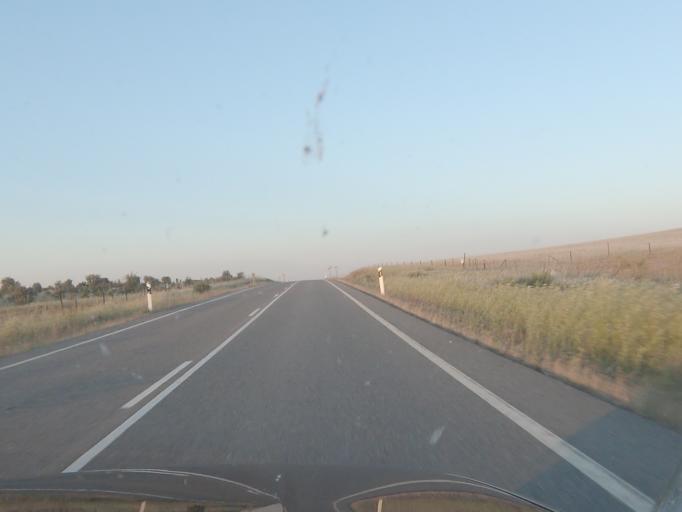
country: ES
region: Extremadura
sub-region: Provincia de Caceres
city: Alcantara
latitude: 39.6145
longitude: -6.9490
